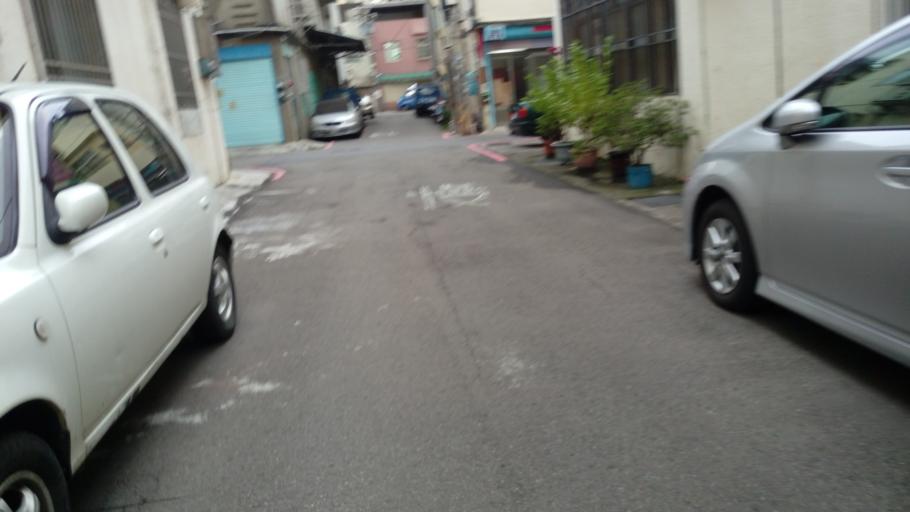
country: TW
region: Taiwan
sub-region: Hsinchu
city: Hsinchu
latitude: 24.8040
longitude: 120.9519
